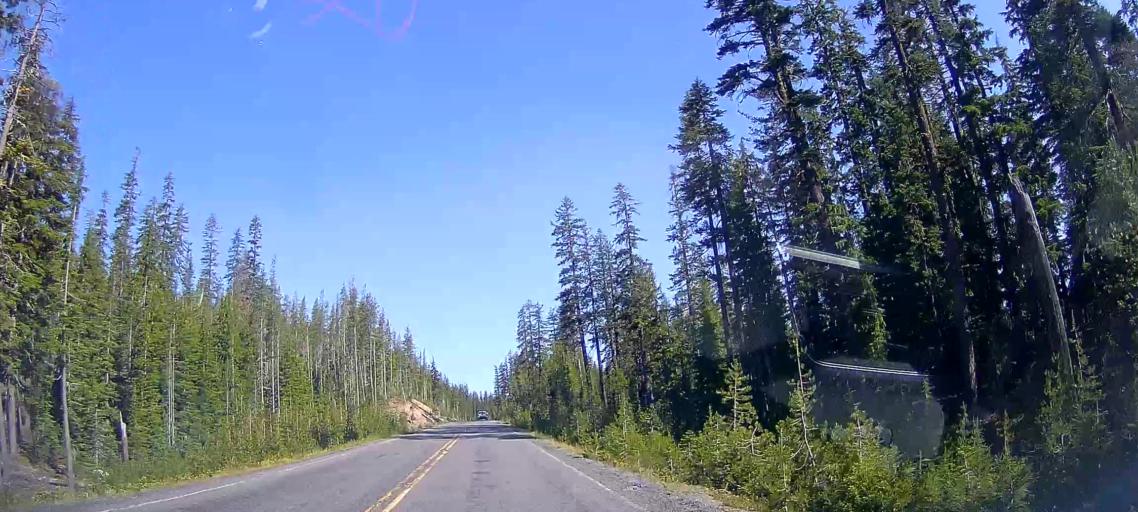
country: US
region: Oregon
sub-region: Jackson County
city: Shady Cove
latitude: 42.8493
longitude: -122.1477
